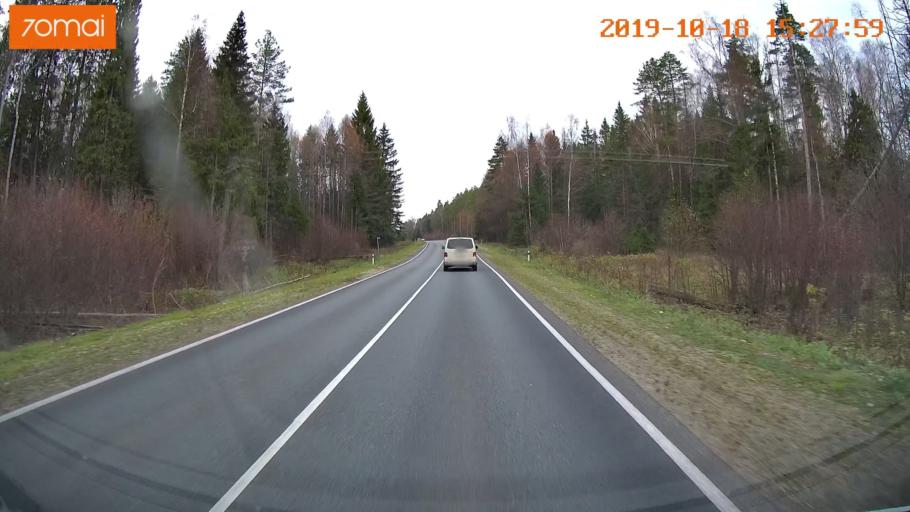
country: RU
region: Vladimir
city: Anopino
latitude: 55.7605
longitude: 40.6730
